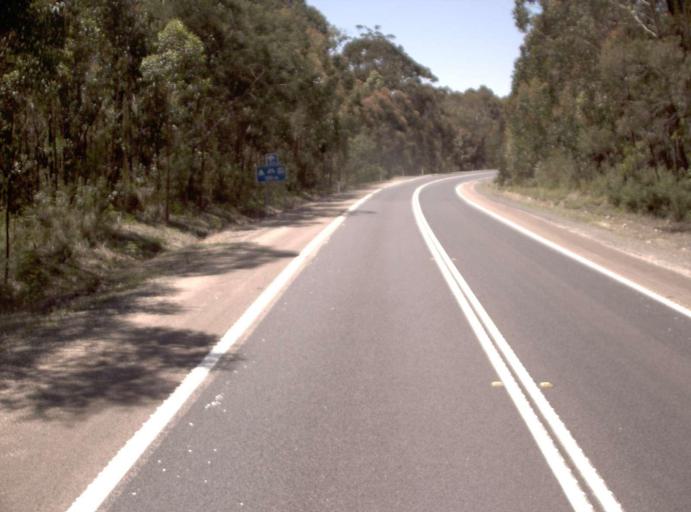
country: AU
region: Victoria
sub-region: East Gippsland
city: Lakes Entrance
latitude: -37.6915
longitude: 148.6156
